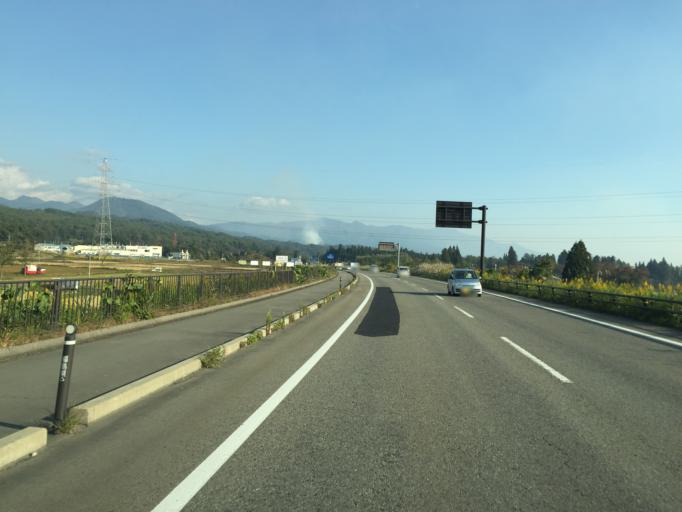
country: JP
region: Fukushima
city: Kitakata
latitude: 37.7046
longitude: 139.8697
